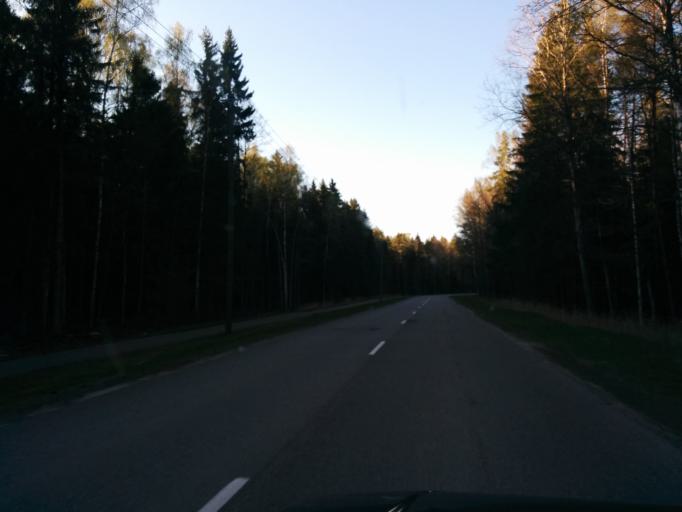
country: LV
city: Tireli
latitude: 56.9585
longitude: 23.5230
